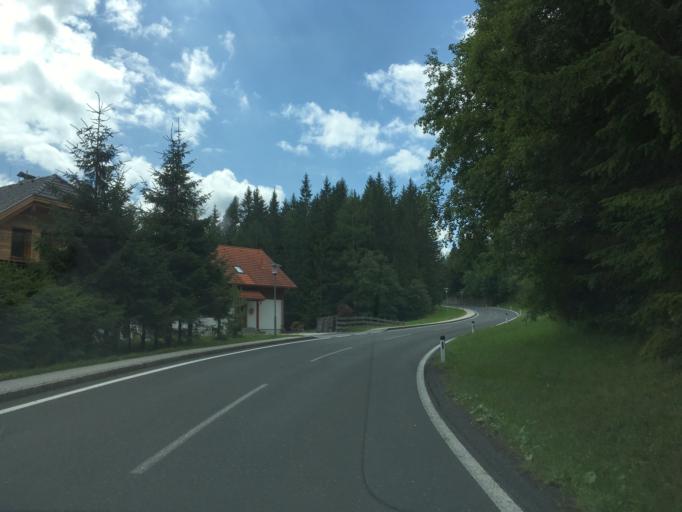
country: AT
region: Carinthia
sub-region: Politischer Bezirk Spittal an der Drau
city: Kleinkirchheim
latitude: 46.8314
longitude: 13.7671
